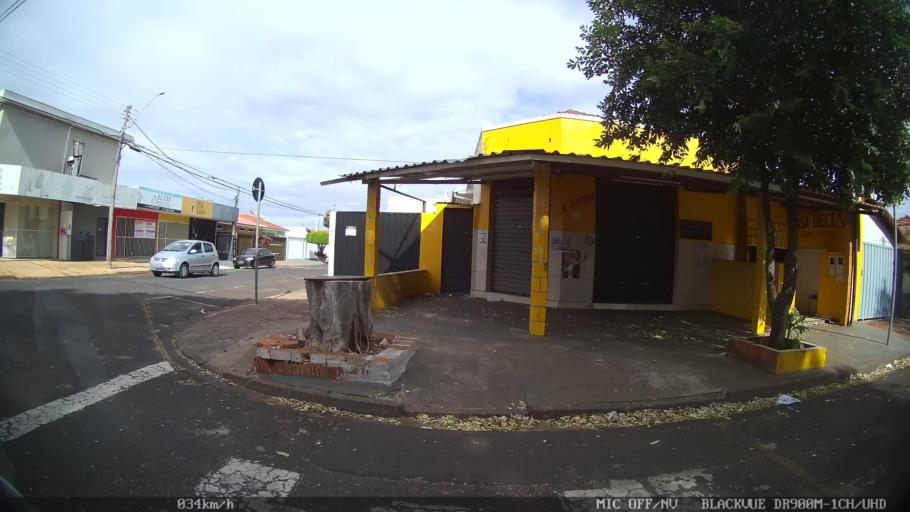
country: BR
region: Sao Paulo
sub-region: Sao Jose Do Rio Preto
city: Sao Jose do Rio Preto
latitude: -20.8325
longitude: -49.3779
